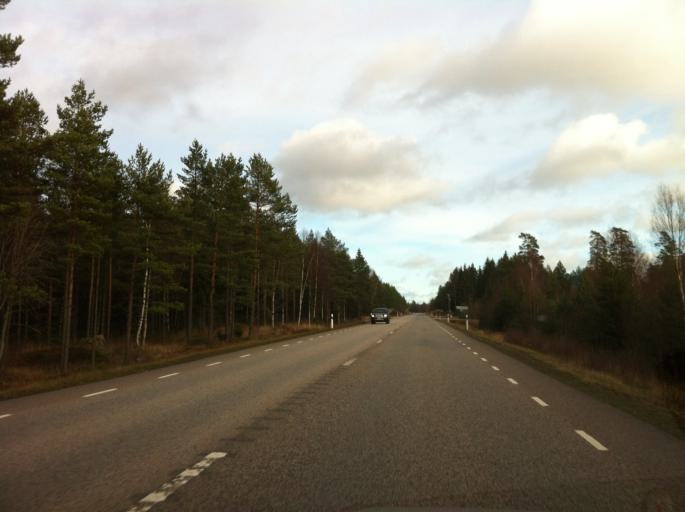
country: SE
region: Kronoberg
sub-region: Uppvidinge Kommun
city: Lenhovda
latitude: 57.1029
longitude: 15.2059
